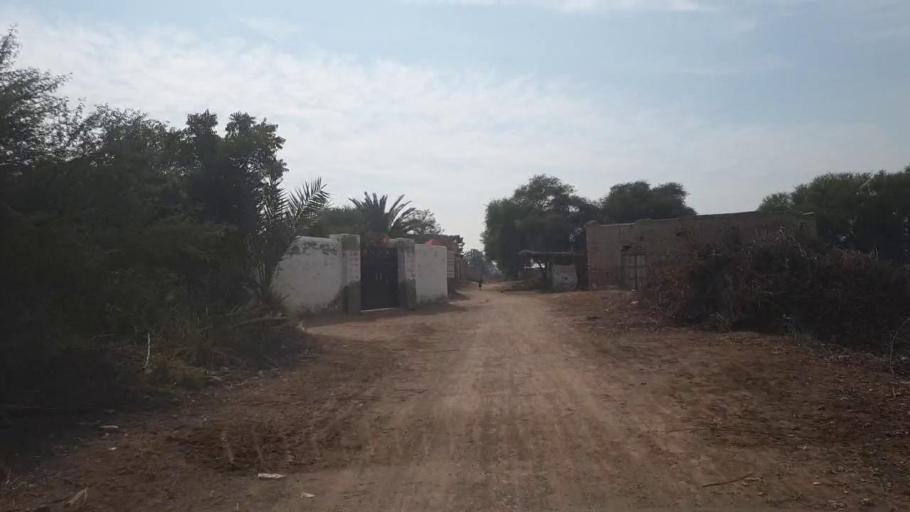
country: PK
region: Sindh
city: Nawabshah
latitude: 26.1197
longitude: 68.4733
